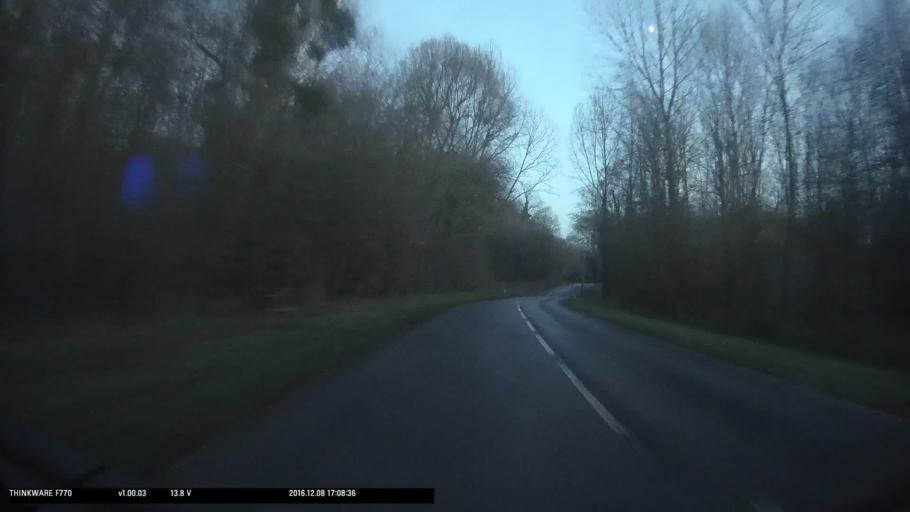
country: FR
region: Ile-de-France
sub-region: Departement du Val-d'Oise
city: Ableiges
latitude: 49.0870
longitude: 1.9931
